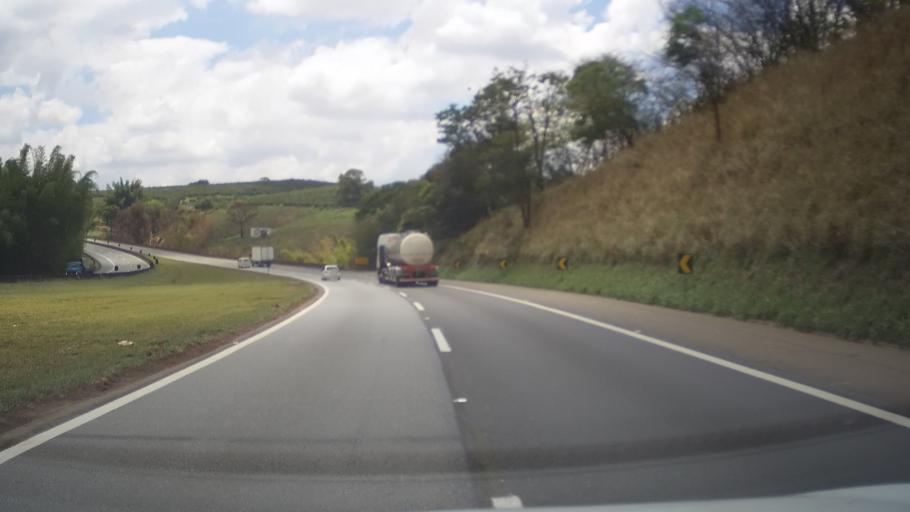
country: BR
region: Minas Gerais
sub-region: Tres Coracoes
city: Tres Coracoes
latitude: -21.7037
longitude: -45.3689
